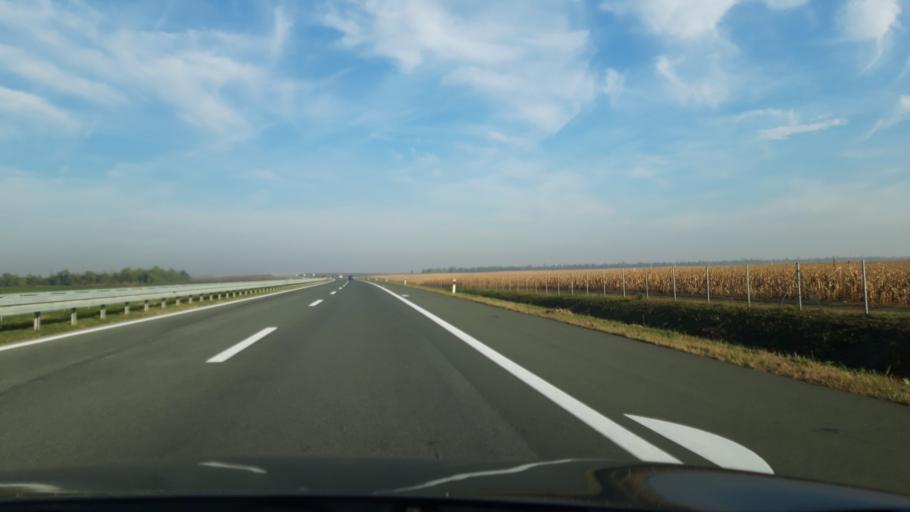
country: RS
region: Autonomna Pokrajina Vojvodina
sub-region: Severnobacki Okrug
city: Mali Igos
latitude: 45.6858
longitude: 19.7274
